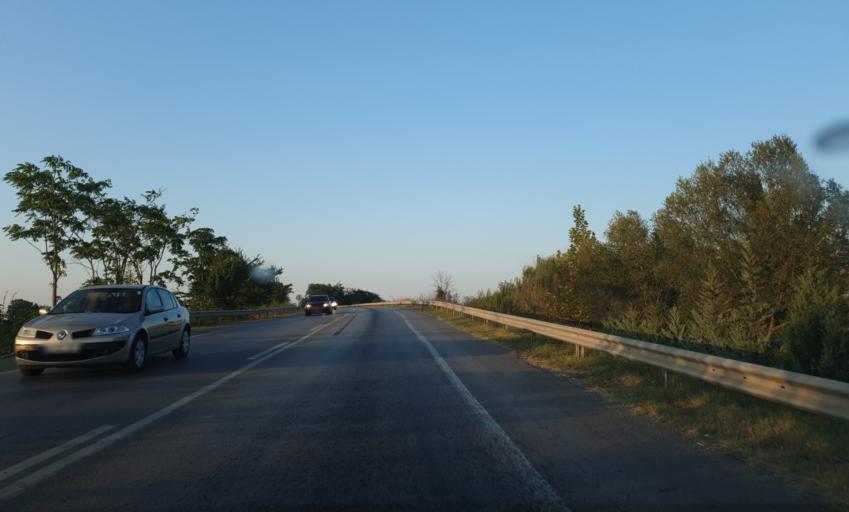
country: TR
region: Kirklareli
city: Luleburgaz
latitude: 41.4474
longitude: 27.3822
